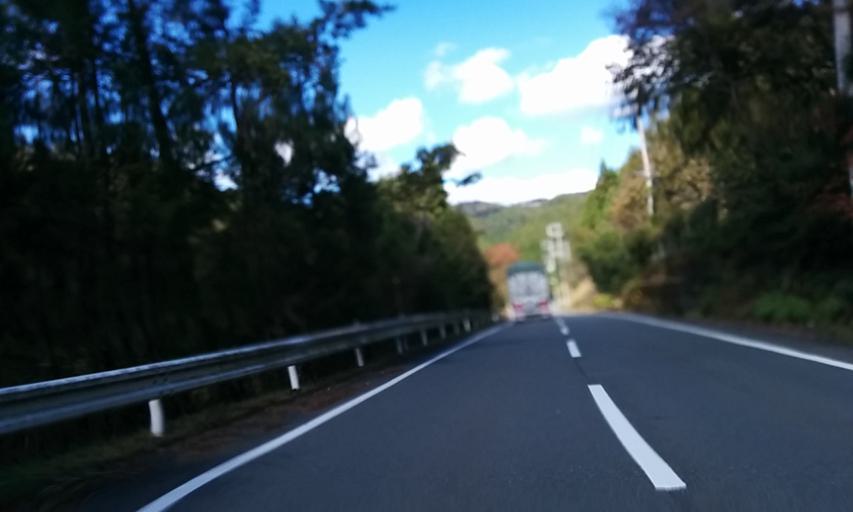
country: JP
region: Kyoto
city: Kameoka
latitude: 35.2001
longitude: 135.6168
